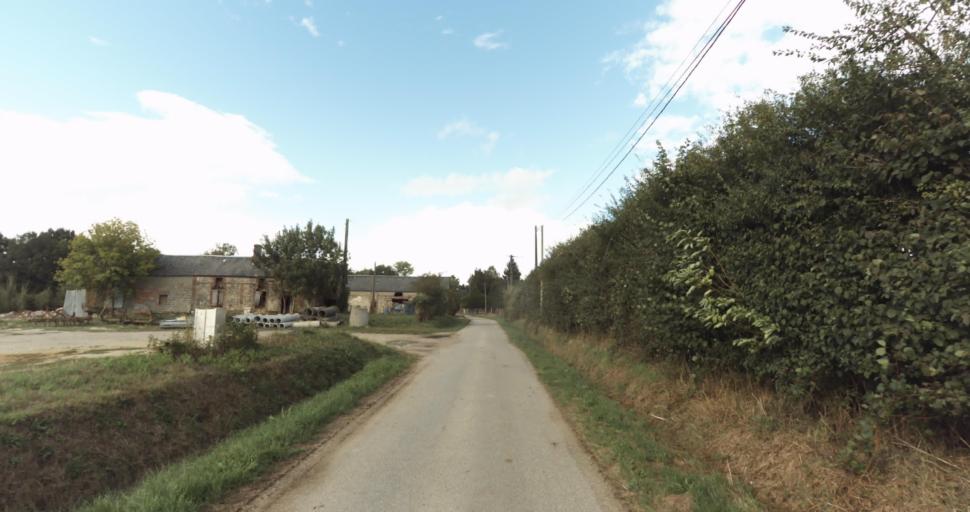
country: FR
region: Lower Normandy
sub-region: Departement de l'Orne
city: Sainte-Gauburge-Sainte-Colombe
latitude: 48.7559
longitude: 0.4017
